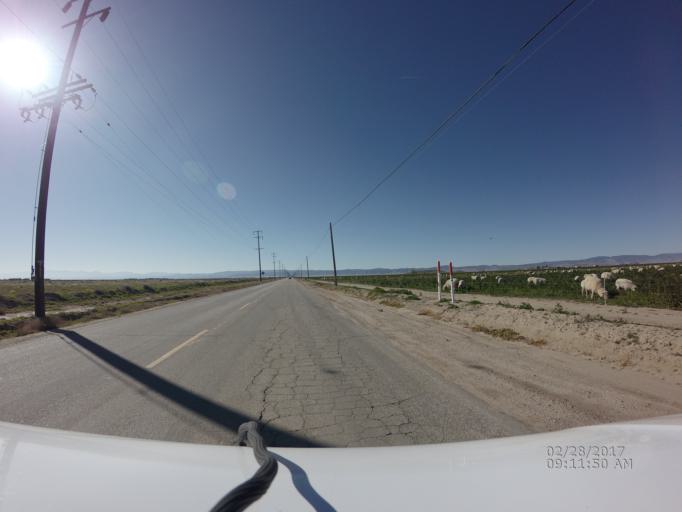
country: US
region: California
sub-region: Kern County
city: Rosamond
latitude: 34.8193
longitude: -118.2905
